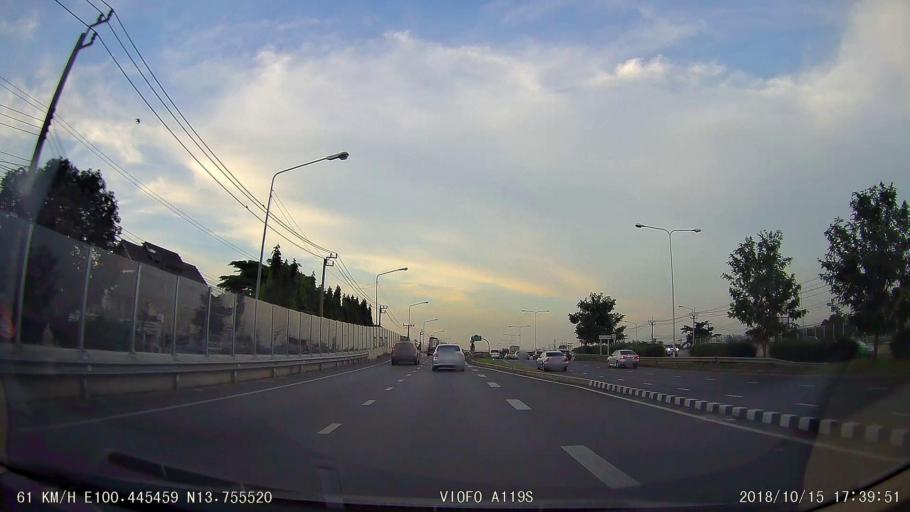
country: TH
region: Bangkok
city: Taling Chan
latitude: 13.7557
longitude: 100.4454
